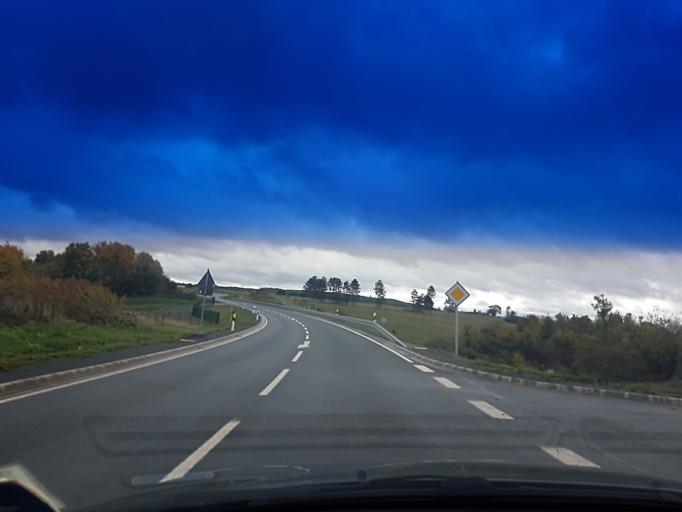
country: DE
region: Bavaria
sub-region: Upper Franconia
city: Bindlach
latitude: 49.9931
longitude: 11.6231
